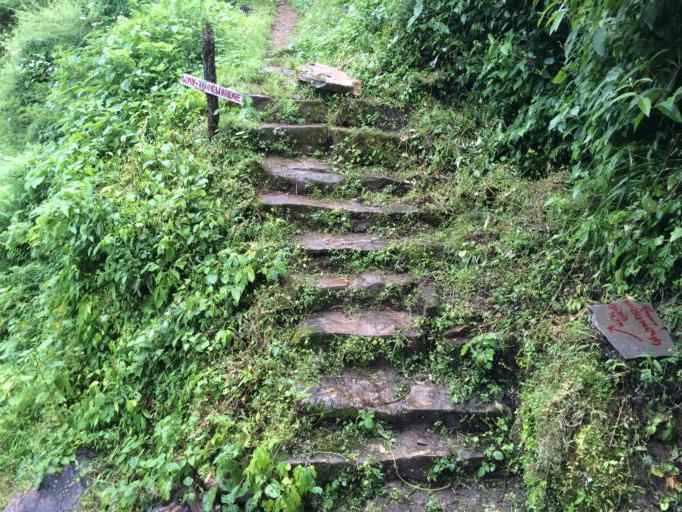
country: NP
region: Western Region
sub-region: Dhawalagiri Zone
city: Chitre
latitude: 28.4067
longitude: 83.8226
